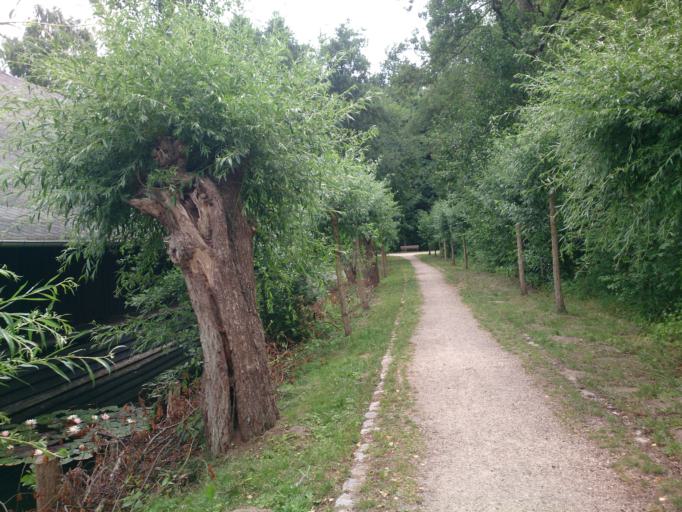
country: DE
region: Mecklenburg-Vorpommern
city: Waren
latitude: 53.5027
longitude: 12.6819
